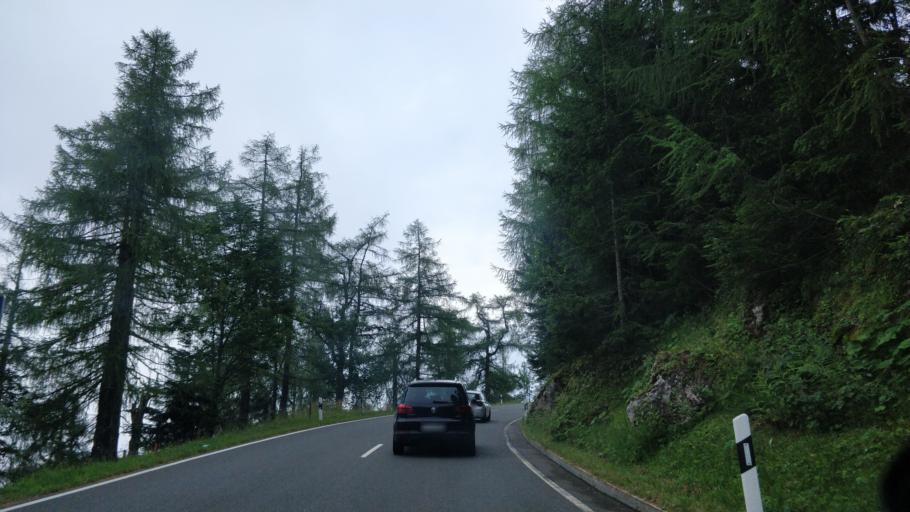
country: AT
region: Salzburg
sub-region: Politischer Bezirk Hallein
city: Hallein
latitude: 47.6329
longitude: 13.0919
